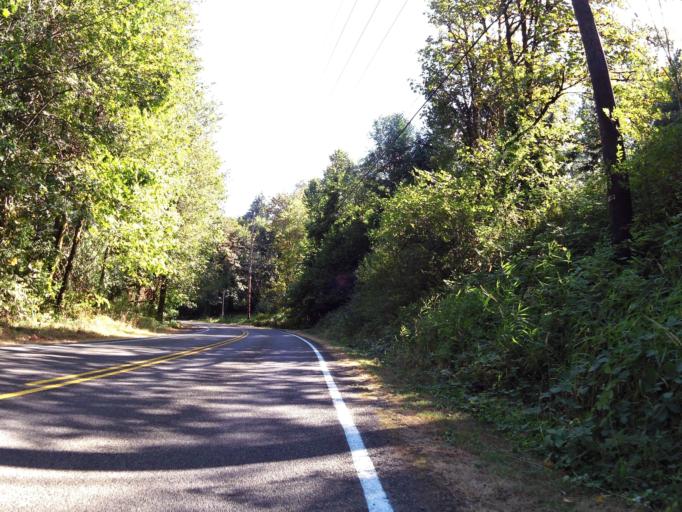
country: US
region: Washington
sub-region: Thurston County
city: Olympia
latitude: 47.0587
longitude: -123.0129
